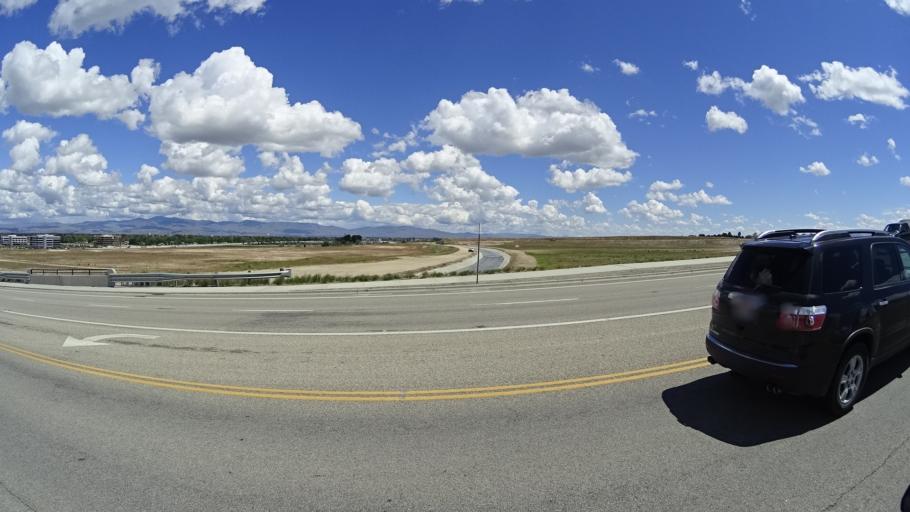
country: US
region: Idaho
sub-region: Ada County
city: Meridian
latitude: 43.5880
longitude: -116.4338
